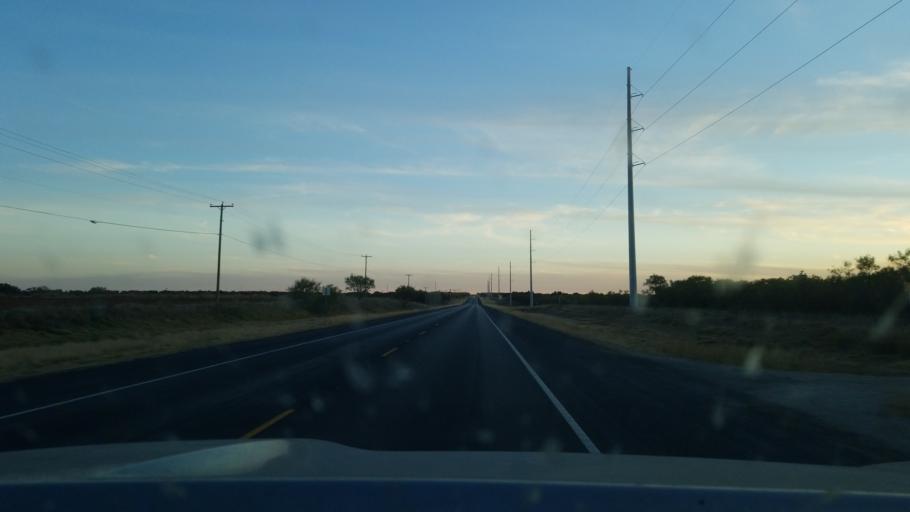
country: US
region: Texas
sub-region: Stephens County
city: Breckenridge
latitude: 32.7080
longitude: -98.9027
